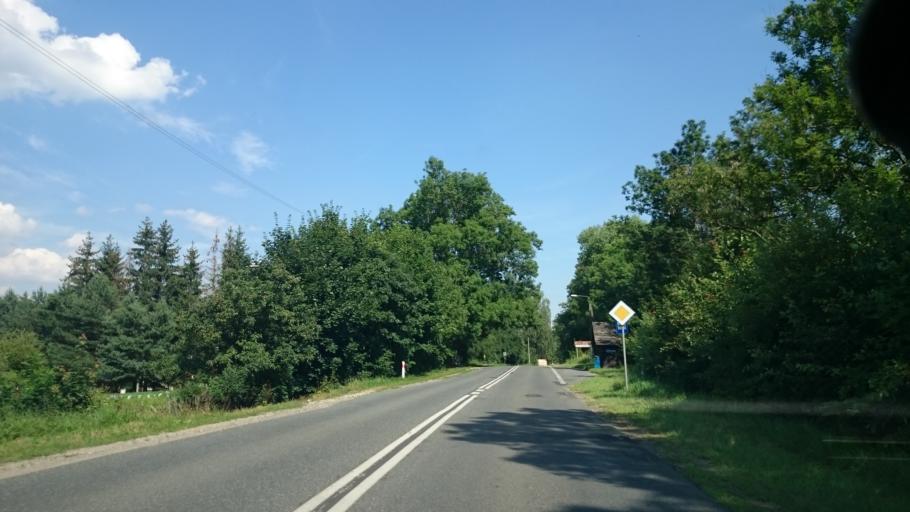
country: PL
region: Lower Silesian Voivodeship
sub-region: Powiat klodzki
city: Ladek-Zdroj
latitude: 50.3397
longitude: 16.8157
